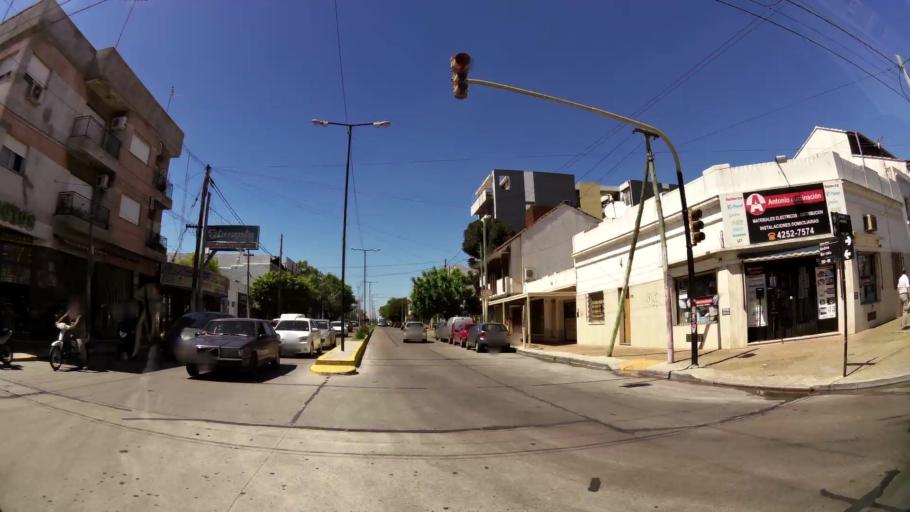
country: AR
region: Buenos Aires
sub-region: Partido de Quilmes
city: Quilmes
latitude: -34.7168
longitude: -58.2755
